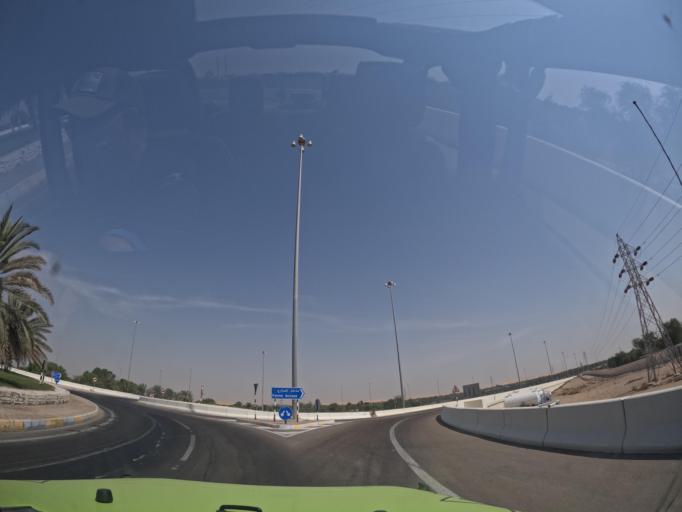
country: AE
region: Abu Dhabi
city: Al Ain
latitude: 24.1749
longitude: 55.1369
